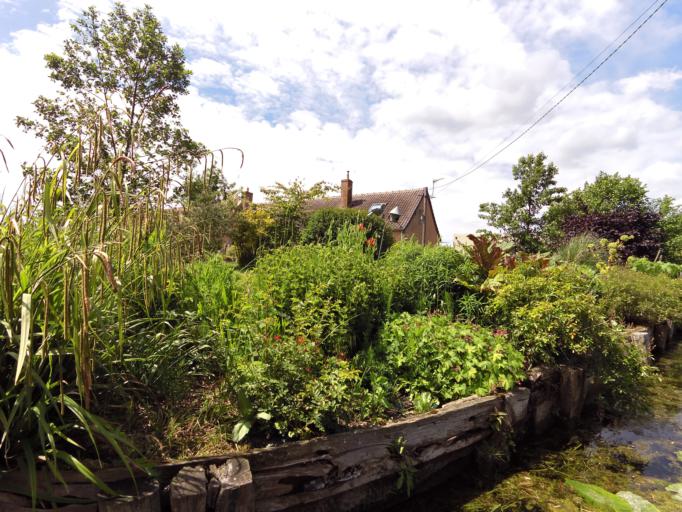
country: FR
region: Nord-Pas-de-Calais
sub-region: Departement du Pas-de-Calais
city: Saint-Martin-au-Laert
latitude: 50.7619
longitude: 2.2442
